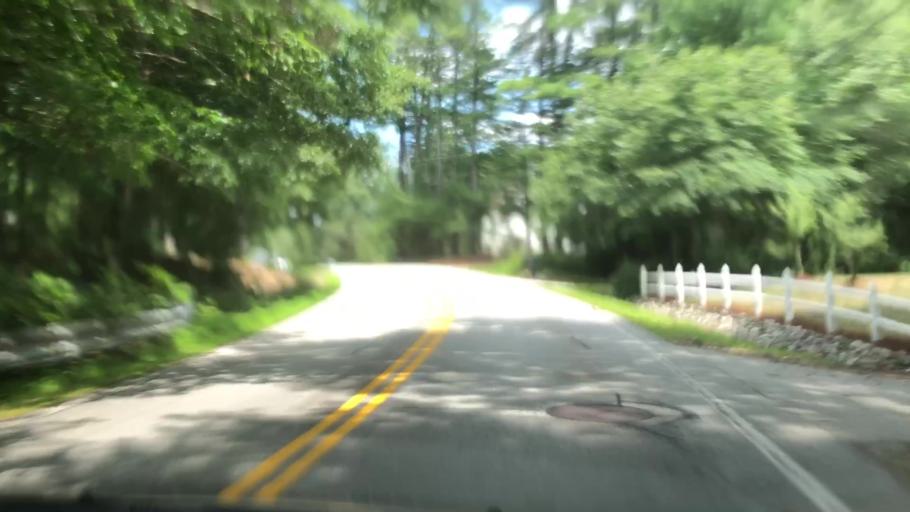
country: US
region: New Hampshire
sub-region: Hillsborough County
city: Bedford
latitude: 42.9380
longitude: -71.4942
